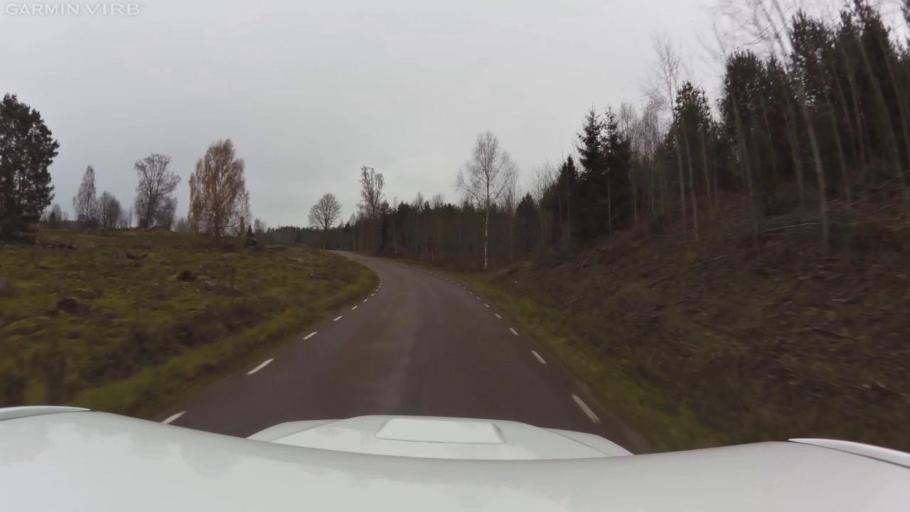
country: SE
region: OEstergoetland
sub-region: Mjolby Kommun
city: Mantorp
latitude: 58.1555
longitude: 15.3899
